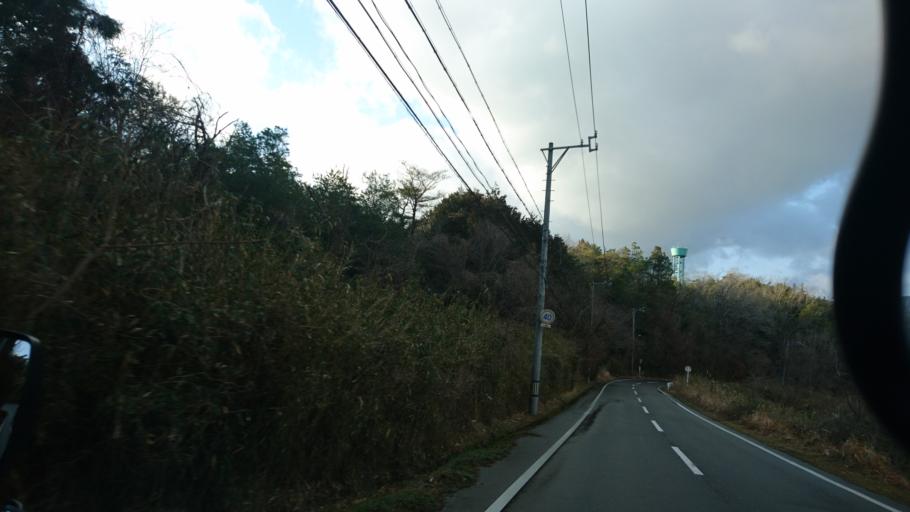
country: JP
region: Mie
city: Ueno-ebisumachi
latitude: 34.7554
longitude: 136.0528
